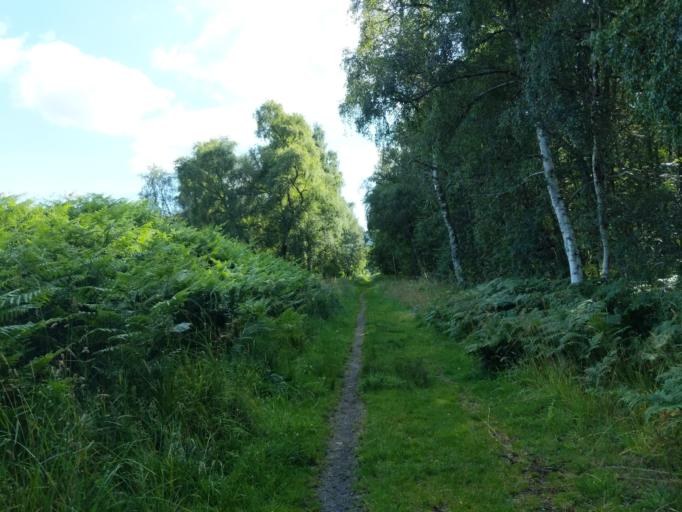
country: GB
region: Scotland
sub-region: Moray
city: Rothes
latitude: 57.4163
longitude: -3.3832
